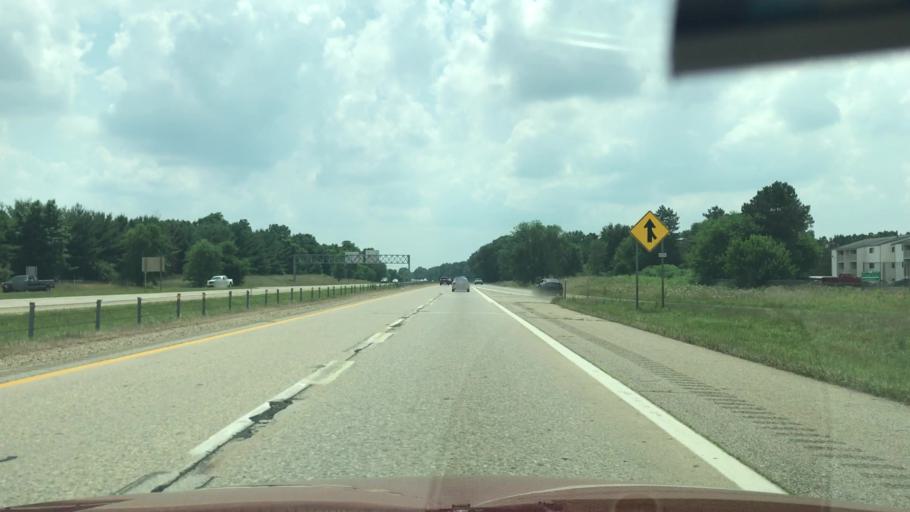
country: US
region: Michigan
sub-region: Allegan County
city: Plainwell
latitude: 42.4466
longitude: -85.6577
